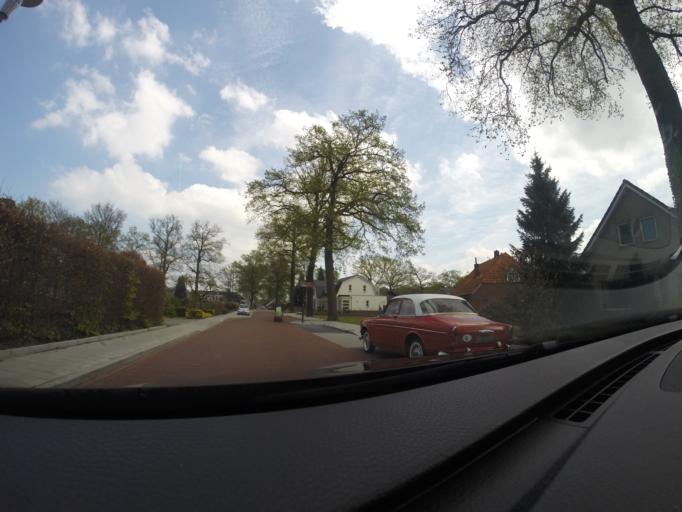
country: NL
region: Gelderland
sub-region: Berkelland
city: Neede
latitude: 52.1127
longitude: 6.5795
